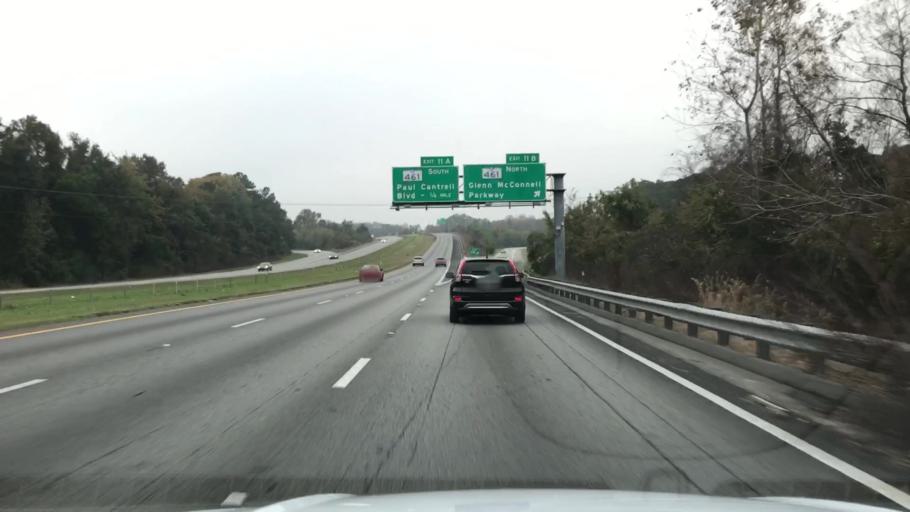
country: US
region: South Carolina
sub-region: Charleston County
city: North Charleston
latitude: 32.8144
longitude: -80.0339
